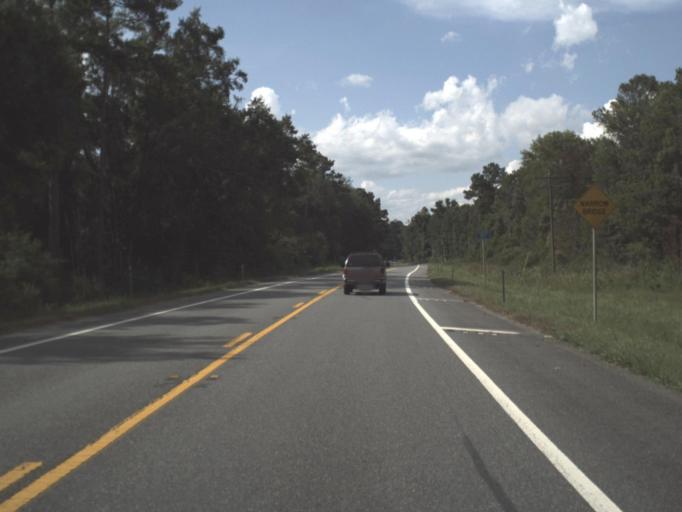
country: US
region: Florida
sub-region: Taylor County
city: Perry
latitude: 30.2815
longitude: -83.6307
